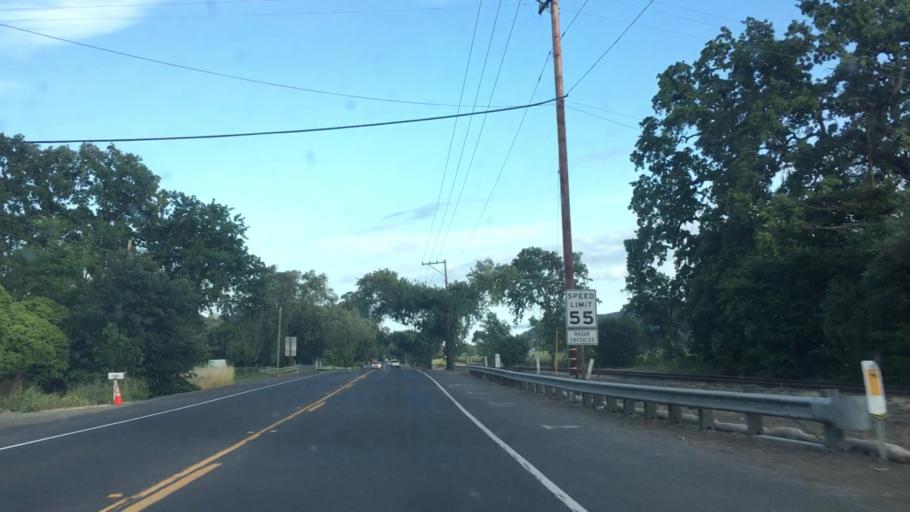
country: US
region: California
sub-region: Napa County
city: Yountville
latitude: 38.4325
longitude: -122.3988
